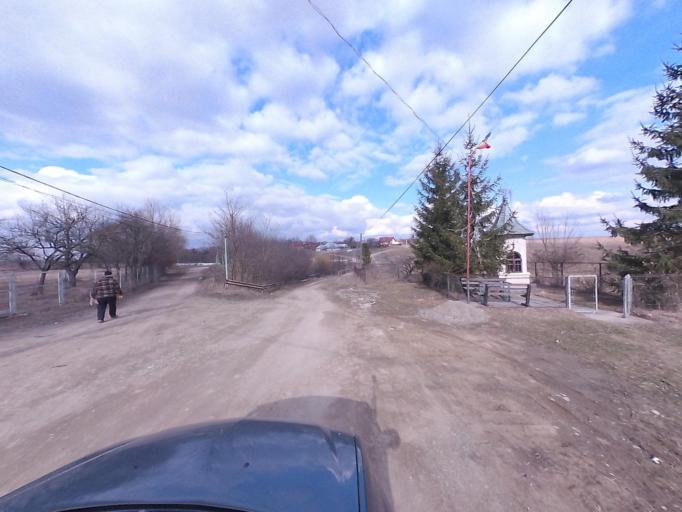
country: RO
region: Neamt
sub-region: Oras Targu Neamt
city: Targu Neamt
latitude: 47.2149
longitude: 26.3807
